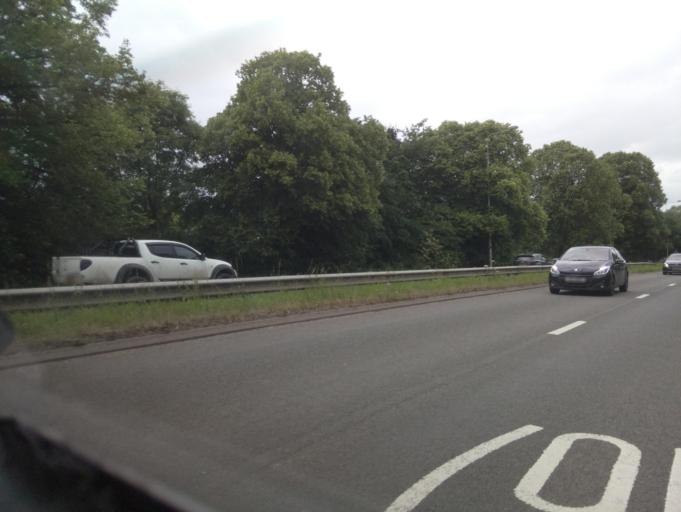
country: GB
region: England
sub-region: Staffordshire
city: Penkridge
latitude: 52.6947
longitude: -2.1308
